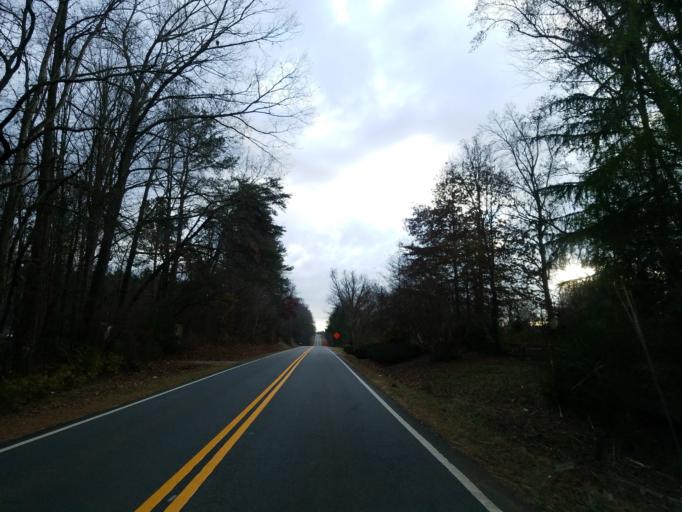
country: US
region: Georgia
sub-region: Dawson County
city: Dawsonville
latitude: 34.3320
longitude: -84.0680
